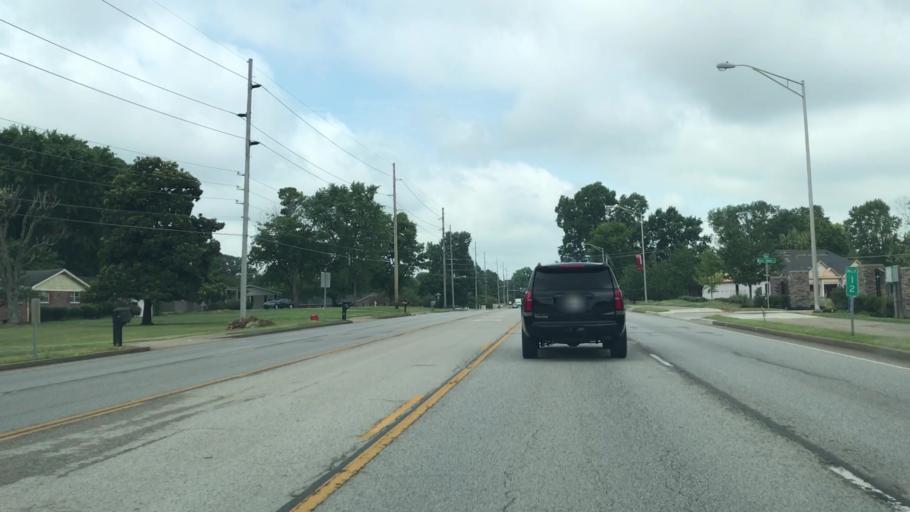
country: US
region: Kentucky
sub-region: Warren County
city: Bowling Green
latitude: 36.9898
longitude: -86.4138
